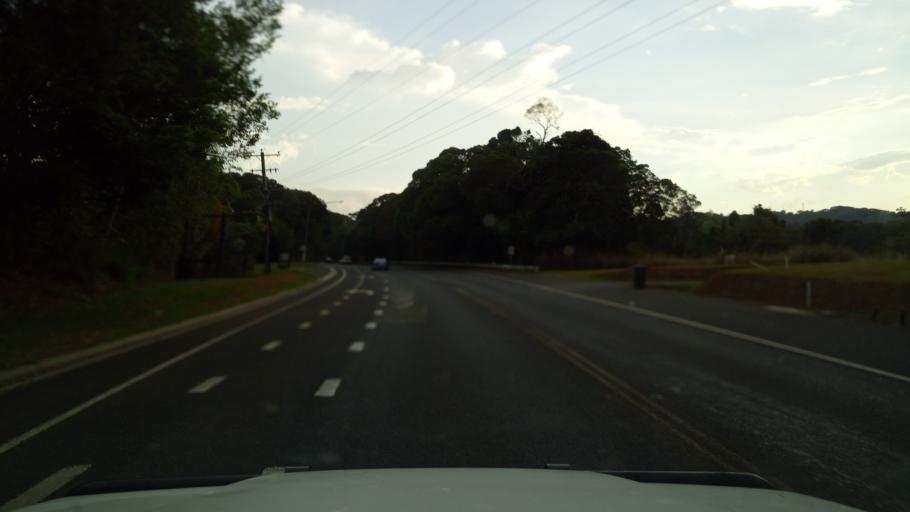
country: AU
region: Queensland
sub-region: Tablelands
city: Kuranda
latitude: -16.8279
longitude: 145.6217
